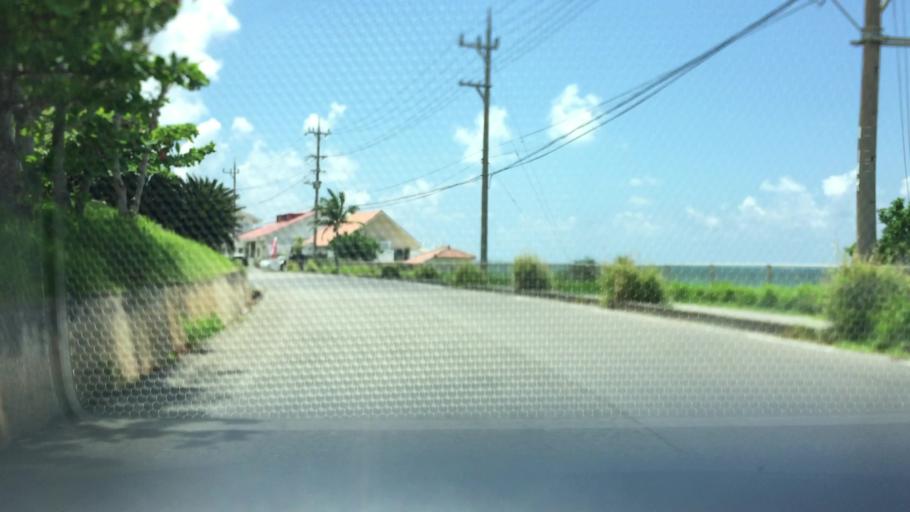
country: JP
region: Okinawa
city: Ishigaki
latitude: 24.3653
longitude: 124.1130
